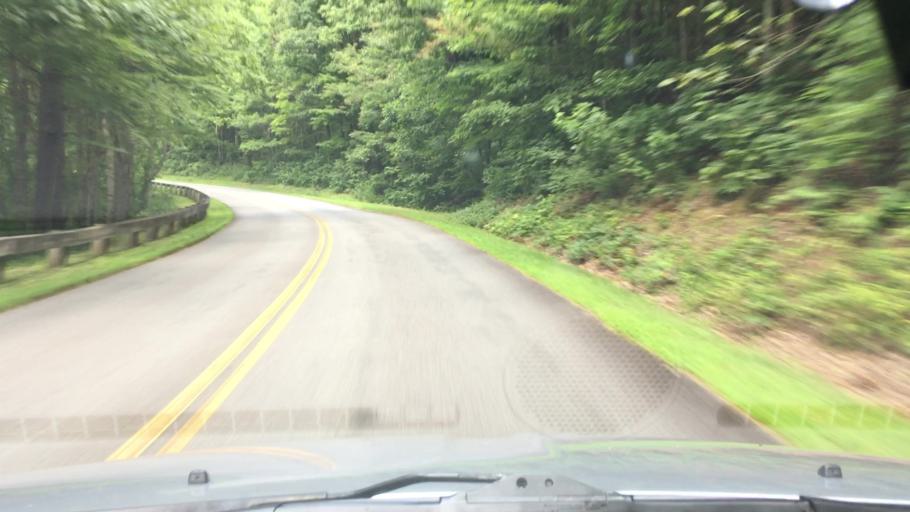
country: US
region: North Carolina
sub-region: Buncombe County
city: Asheville
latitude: 35.6223
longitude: -82.4928
